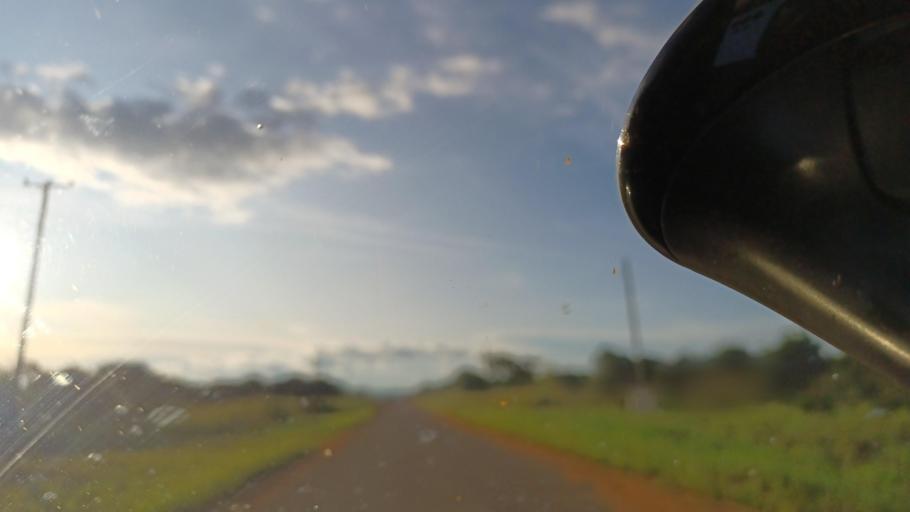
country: ZM
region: North-Western
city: Kasempa
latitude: -13.4643
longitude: 25.8555
